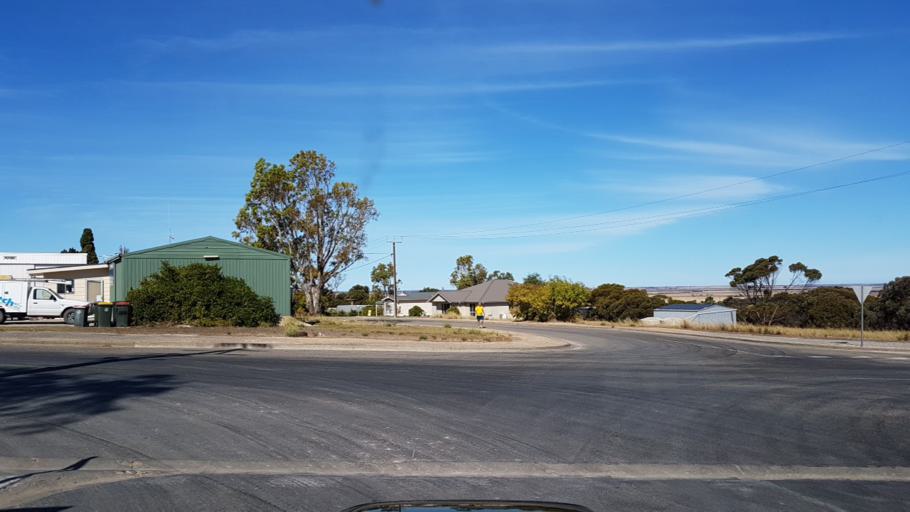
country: AU
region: South Australia
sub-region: Yorke Peninsula
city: Honiton
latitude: -34.9924
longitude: 137.4009
